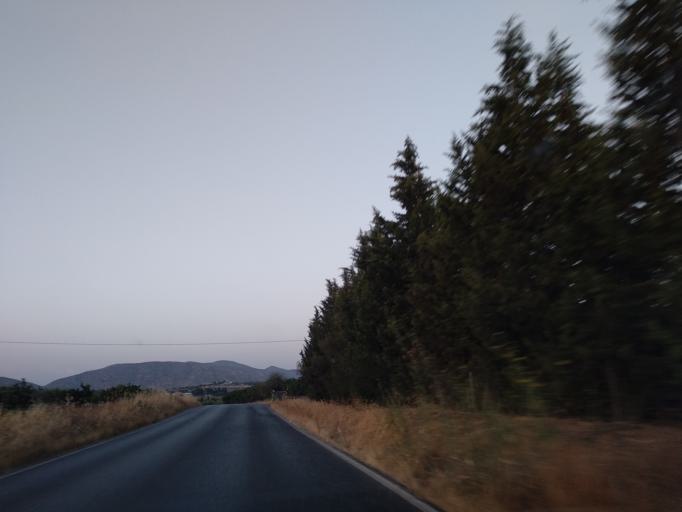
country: ES
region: Andalusia
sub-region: Provincia de Malaga
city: Alhaurin el Grande
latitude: 36.6691
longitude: -4.6668
